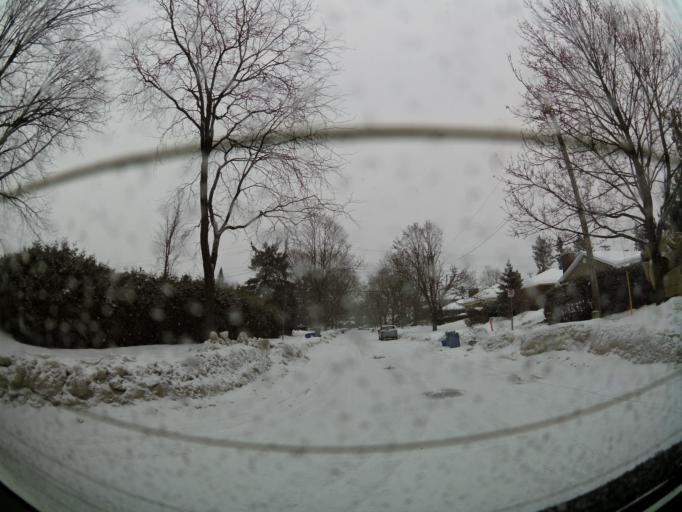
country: CA
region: Ontario
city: Ottawa
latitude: 45.4078
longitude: -75.6431
